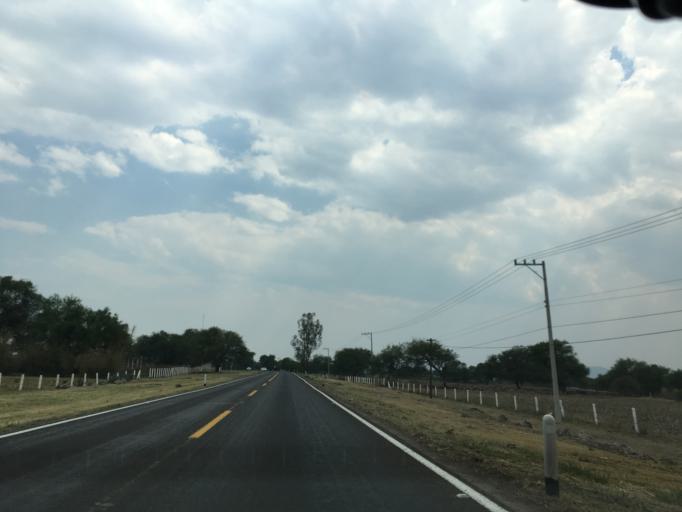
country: MX
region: Michoacan
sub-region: Cuitzeo
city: Cuamio
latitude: 20.0031
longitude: -101.1557
